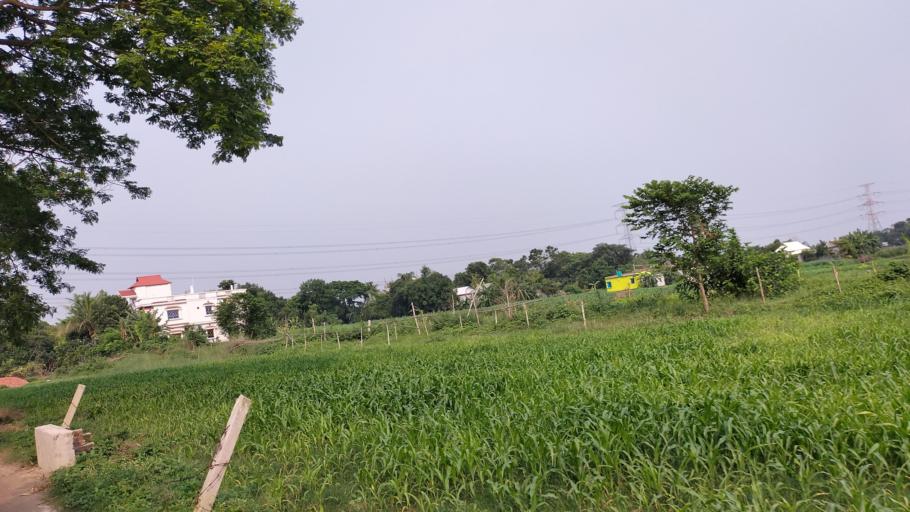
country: BD
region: Dhaka
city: Azimpur
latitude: 23.6679
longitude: 90.3181
